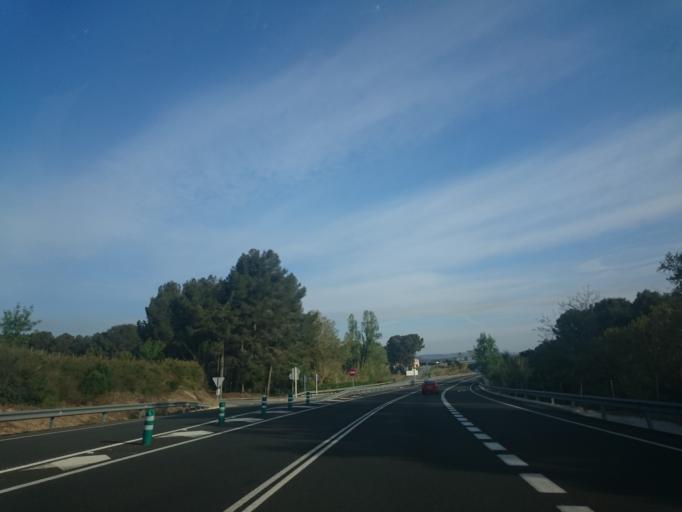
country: ES
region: Catalonia
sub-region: Provincia de Barcelona
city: el Pla del Penedes
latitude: 41.4128
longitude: 1.6978
